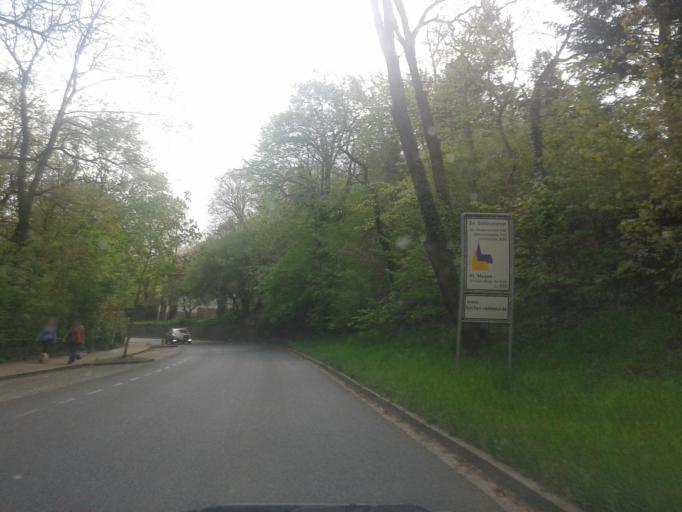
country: DE
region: Saxony
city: Radebeul
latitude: 51.1182
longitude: 13.6311
